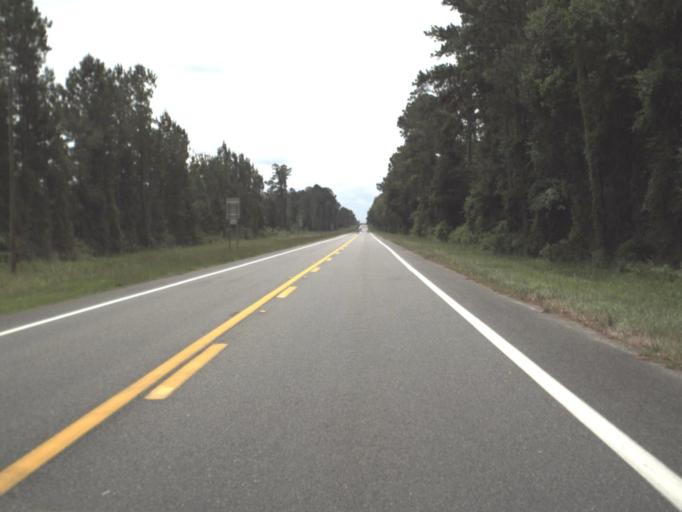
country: US
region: Florida
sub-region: Union County
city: Lake Butler
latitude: 30.0897
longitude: -82.4654
